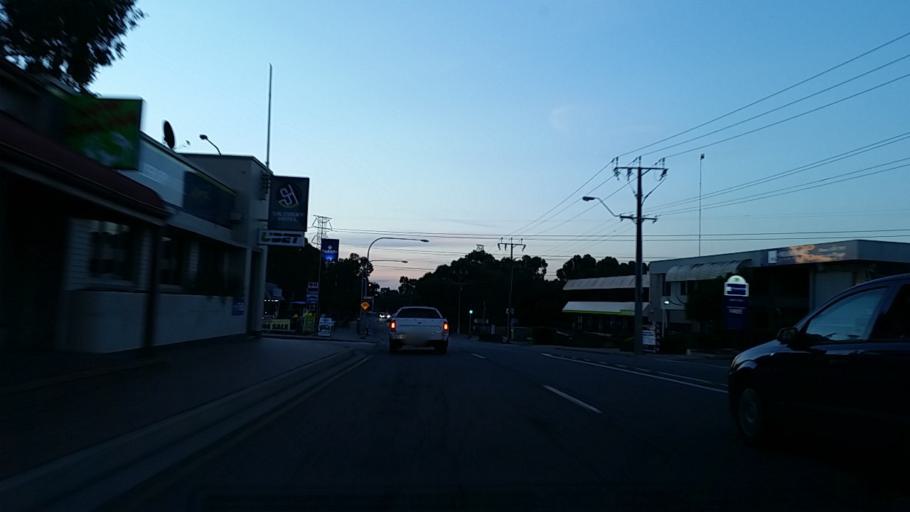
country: AU
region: South Australia
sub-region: Salisbury
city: Salisbury
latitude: -34.7615
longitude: 138.6493
